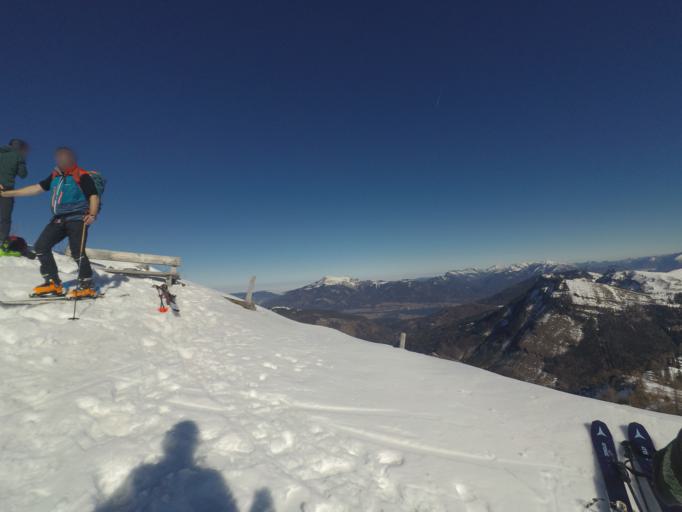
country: AT
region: Salzburg
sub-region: Politischer Bezirk Salzburg-Umgebung
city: Hintersee
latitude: 47.6663
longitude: 13.3749
